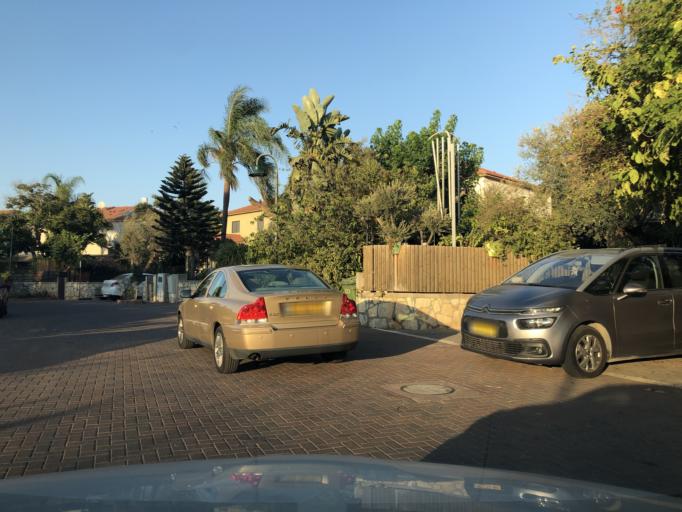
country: PS
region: West Bank
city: Hablah
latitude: 32.1589
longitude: 34.9712
